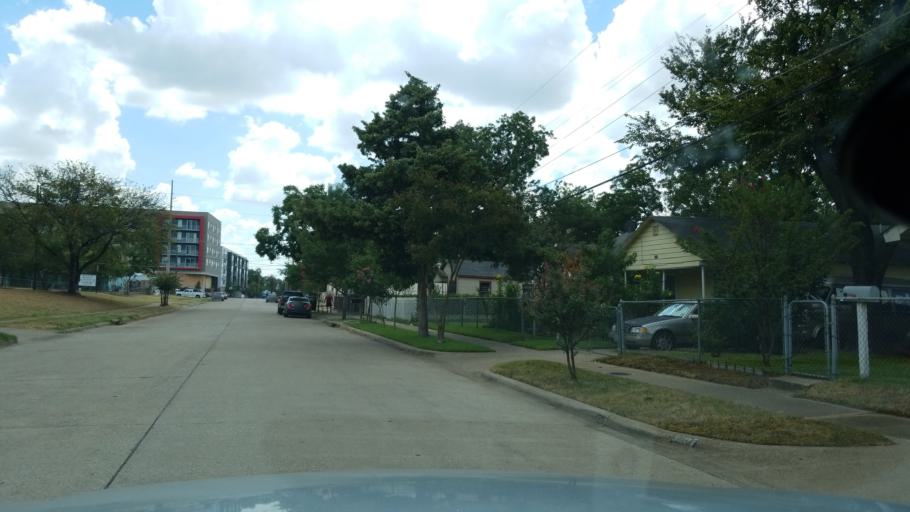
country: US
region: Texas
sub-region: Dallas County
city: Dallas
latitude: 32.7803
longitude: -96.8321
